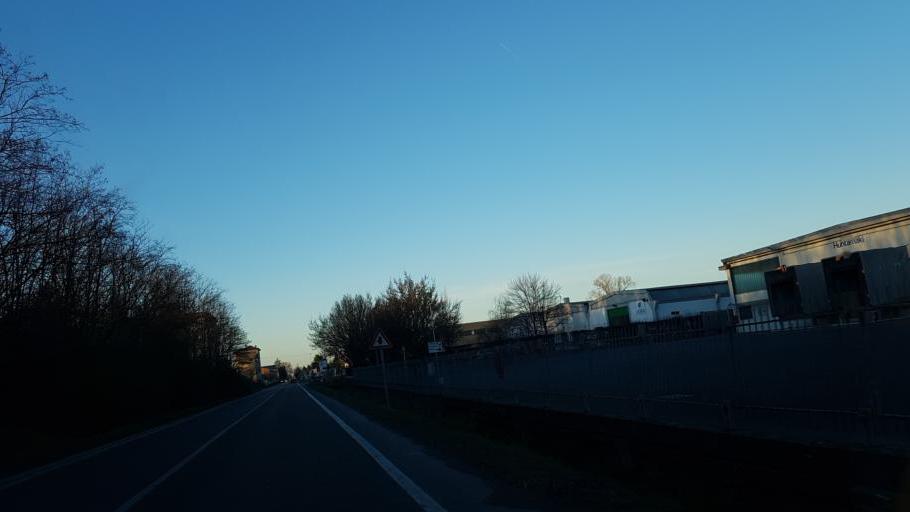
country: IT
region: Piedmont
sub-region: Provincia di Alessandria
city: Carbonara Scrivia
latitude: 44.8542
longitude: 8.8543
